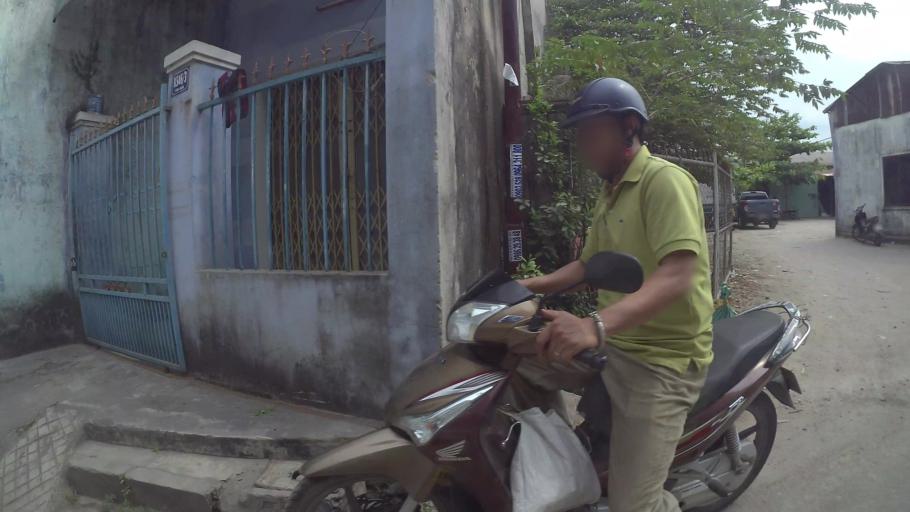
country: VN
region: Da Nang
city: Cam Le
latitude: 16.0391
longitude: 108.1836
